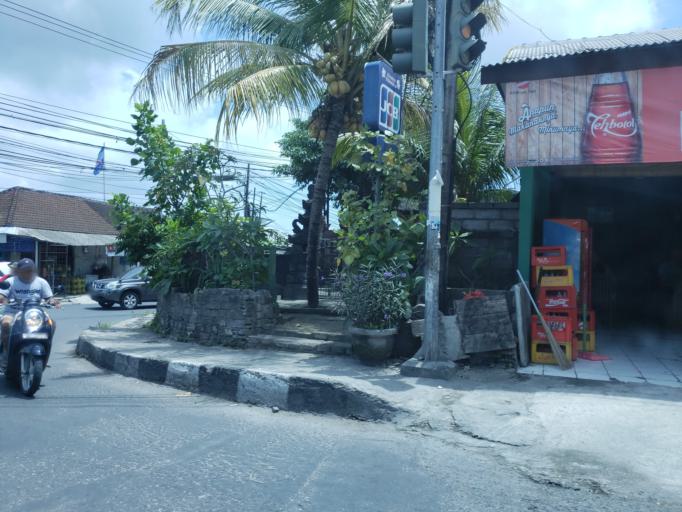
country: ID
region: Bali
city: Jimbaran
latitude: -8.8158
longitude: 115.1559
